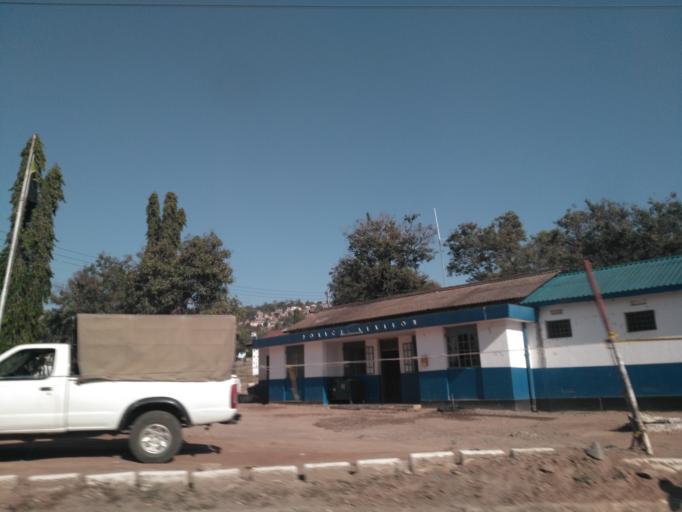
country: TZ
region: Mwanza
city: Mwanza
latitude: -2.5025
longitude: 32.8956
